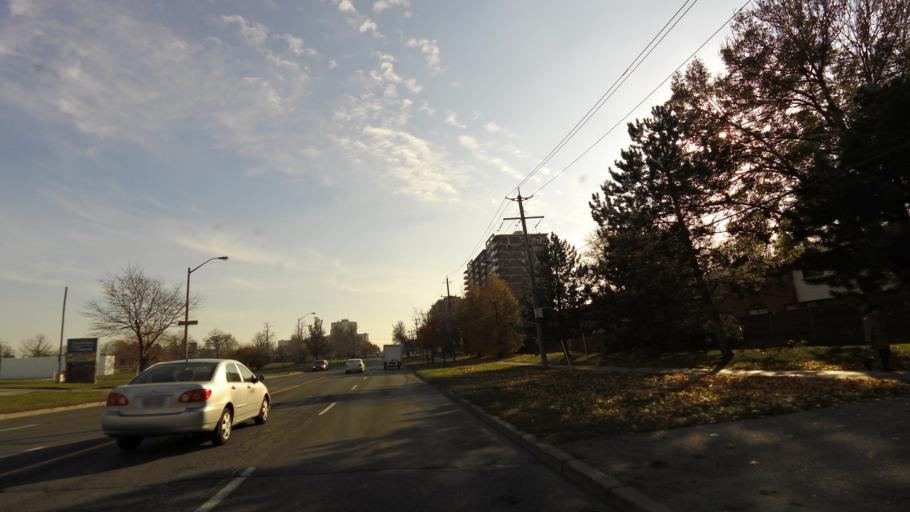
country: CA
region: Ontario
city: Concord
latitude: 43.7683
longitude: -79.5203
